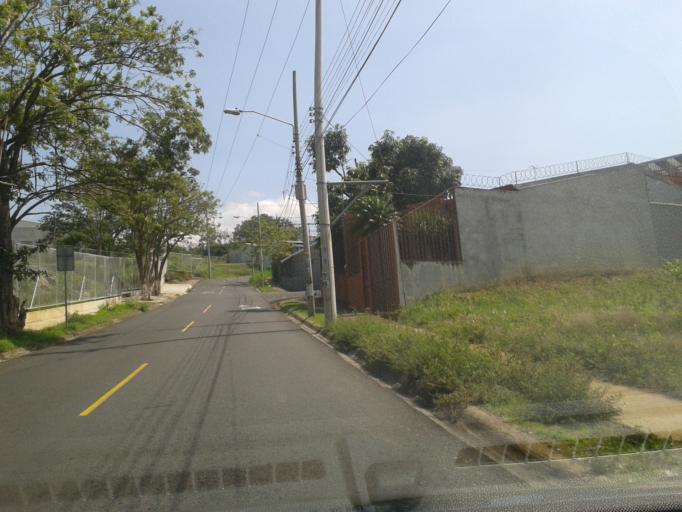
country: CR
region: Heredia
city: San Francisco
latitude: 9.9815
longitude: -84.1381
